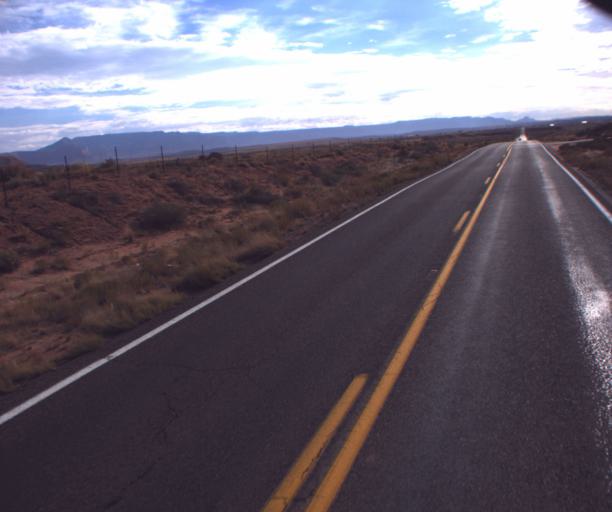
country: US
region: Arizona
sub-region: Apache County
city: Many Farms
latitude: 36.5337
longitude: -109.5119
